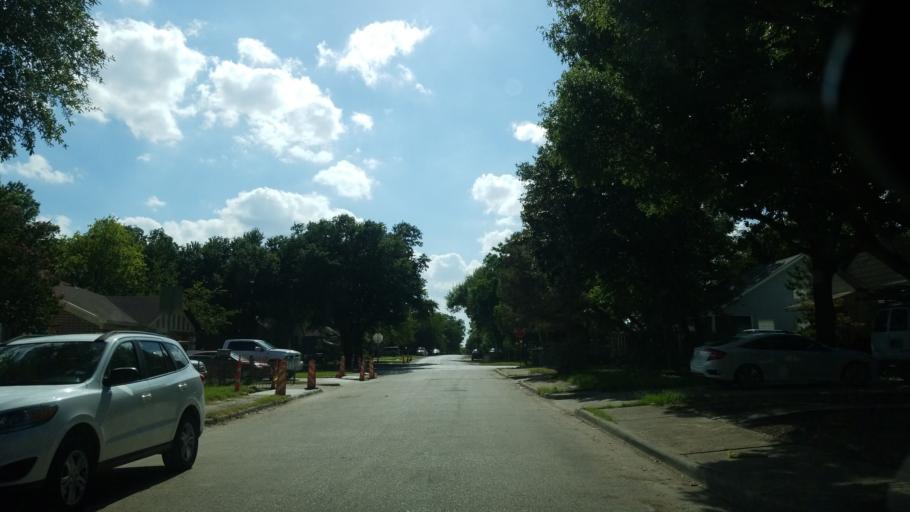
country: US
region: Texas
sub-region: Dallas County
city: Balch Springs
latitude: 32.7692
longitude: -96.7044
